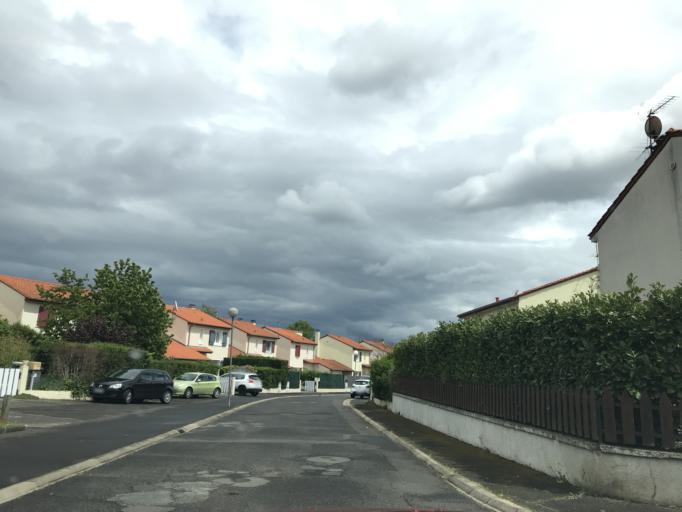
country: FR
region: Auvergne
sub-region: Departement du Puy-de-Dome
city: Pont-du-Chateau
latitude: 45.7926
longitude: 3.2379
